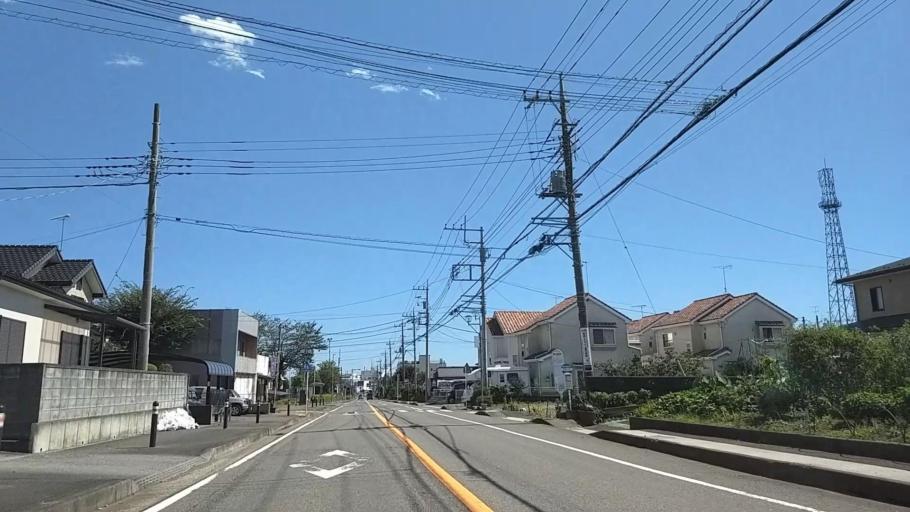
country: JP
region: Kanagawa
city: Zama
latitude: 35.5322
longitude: 139.3156
